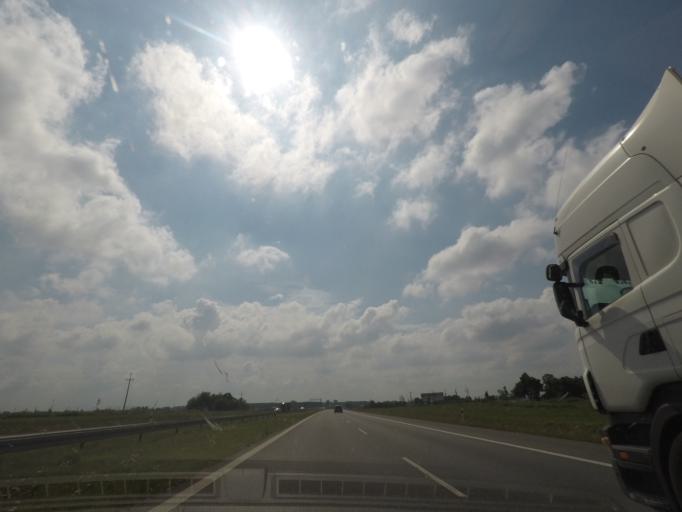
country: PL
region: Lodz Voivodeship
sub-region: Powiat kutnowski
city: Krzyzanow
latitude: 52.2097
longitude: 19.4808
